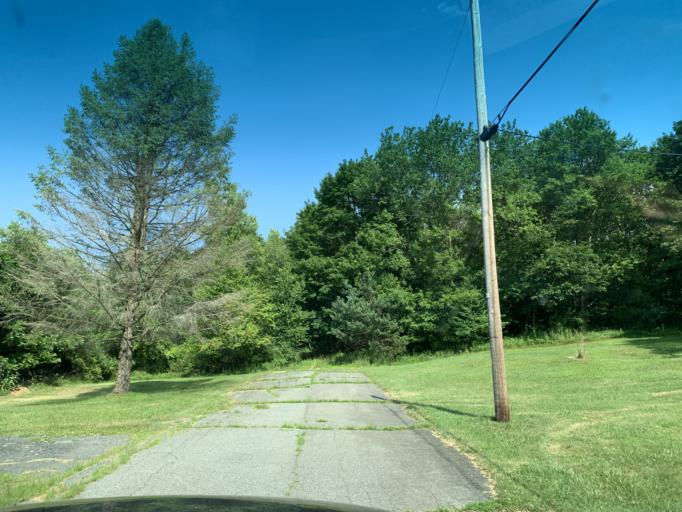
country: US
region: Pennsylvania
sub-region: Schuylkill County
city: Ashland
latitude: 40.8024
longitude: -76.3373
